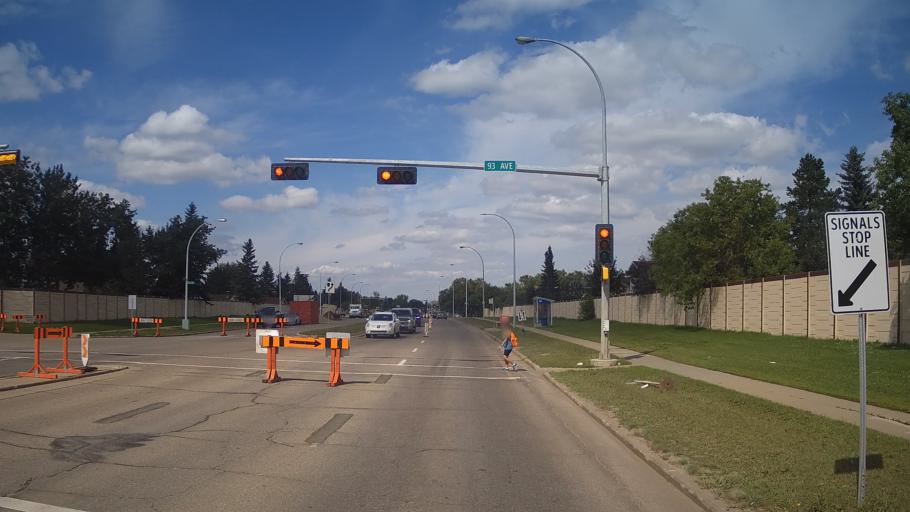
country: CA
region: Alberta
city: St. Albert
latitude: 53.5260
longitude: -113.6299
